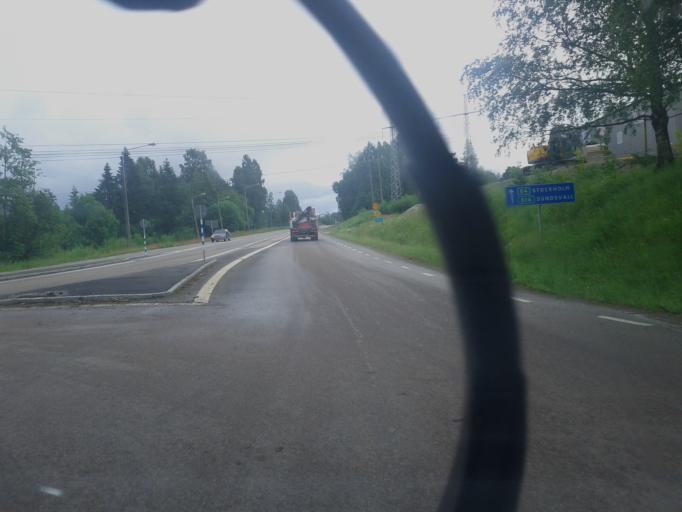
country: SE
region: Vaesternorrland
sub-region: Sundsvalls Kommun
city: Sundsvall
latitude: 62.3987
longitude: 17.2420
